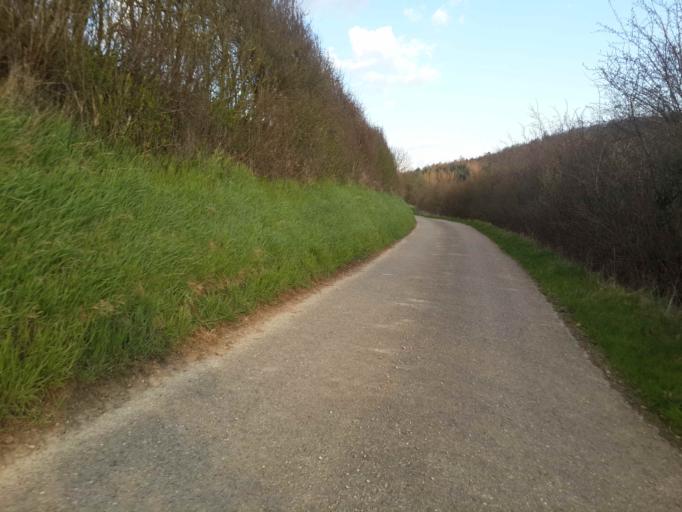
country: DE
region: Baden-Wuerttemberg
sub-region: Regierungsbezirk Stuttgart
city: Ittlingen
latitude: 49.2325
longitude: 8.9342
